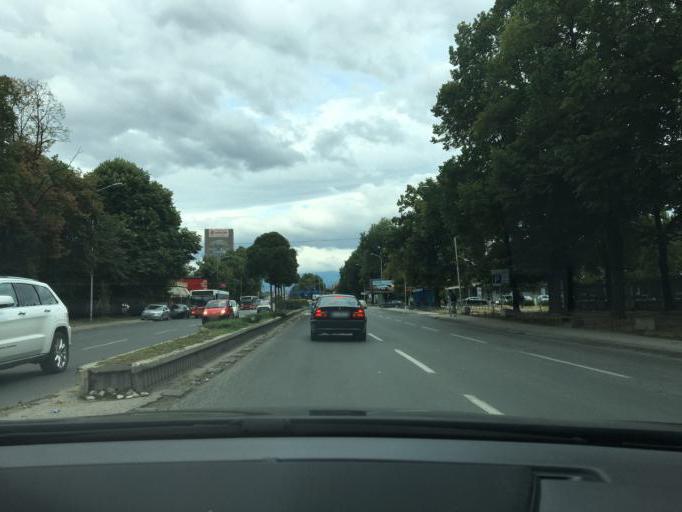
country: MK
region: Karpos
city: Skopje
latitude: 41.9962
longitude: 21.4408
